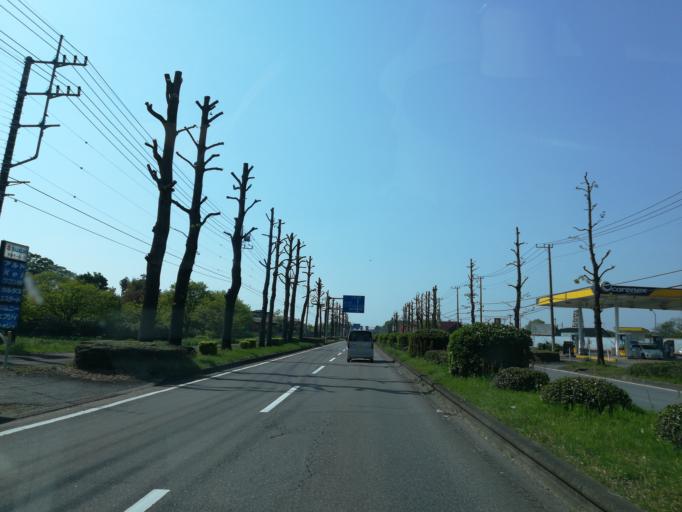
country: JP
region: Ibaraki
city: Naka
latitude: 36.0990
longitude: 140.0912
